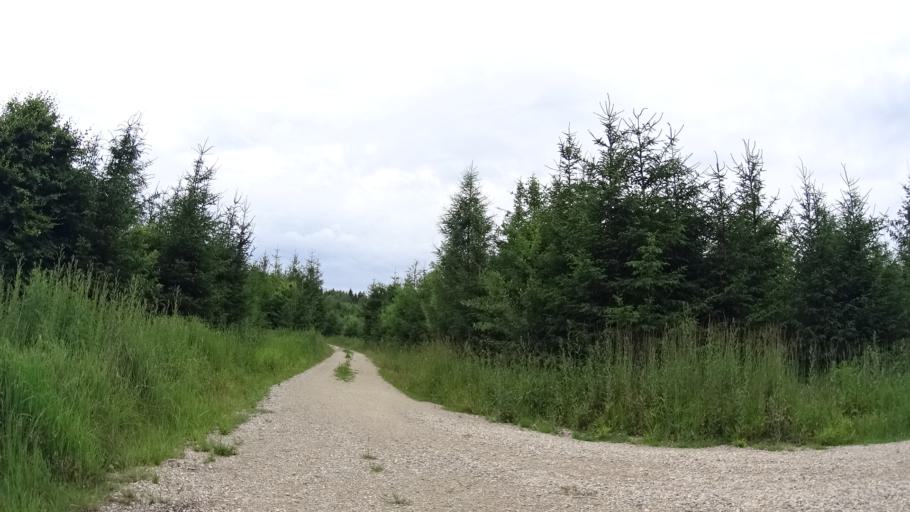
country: DE
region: Bavaria
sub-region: Upper Bavaria
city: Denkendorf
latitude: 48.8993
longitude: 11.4456
